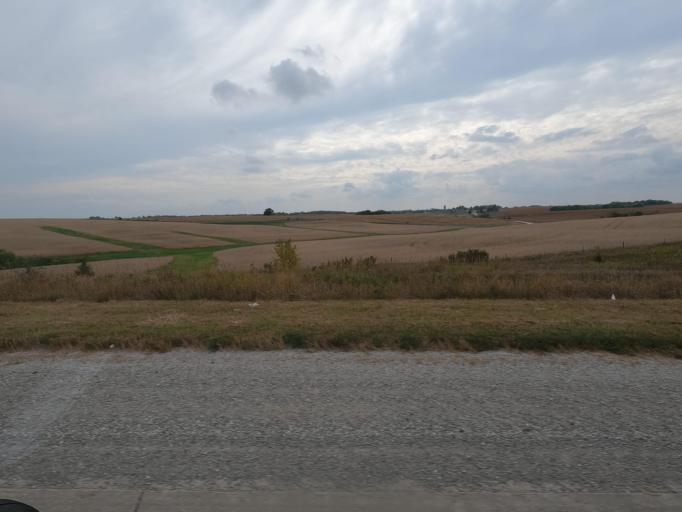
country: US
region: Iowa
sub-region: Jasper County
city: Monroe
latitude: 41.5113
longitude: -93.1205
